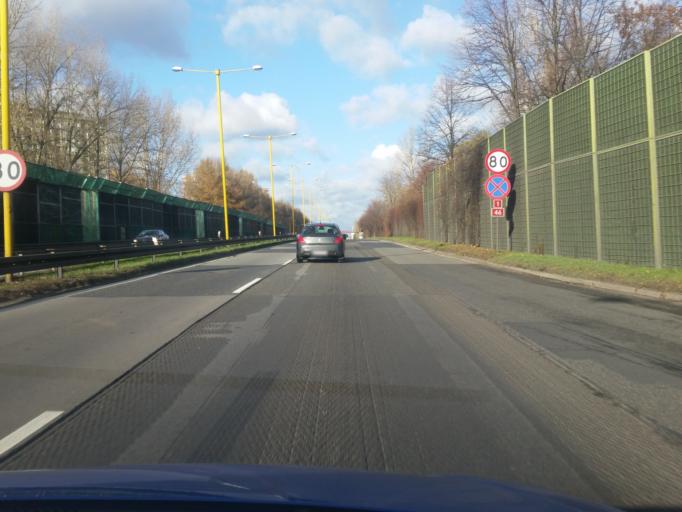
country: PL
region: Silesian Voivodeship
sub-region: Czestochowa
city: Czestochowa
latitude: 50.7735
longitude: 19.1554
